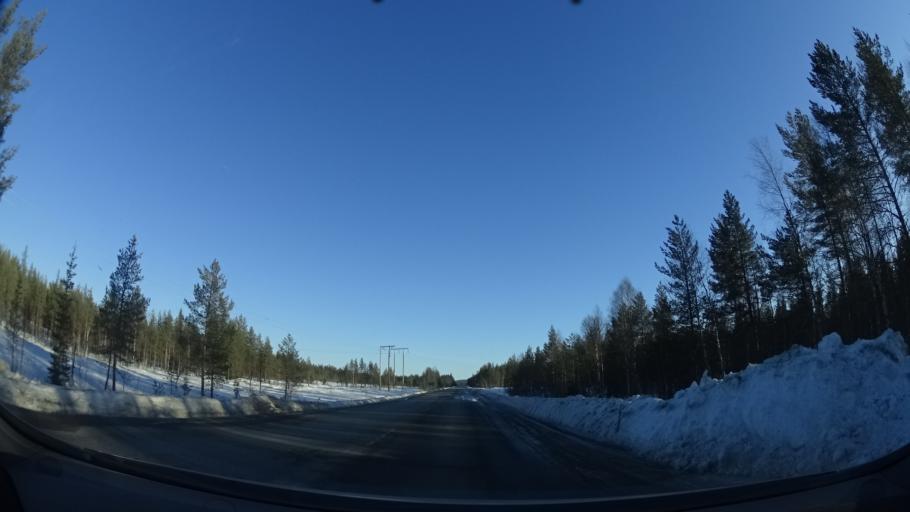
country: SE
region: Vaesterbotten
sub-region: Skelleftea Kommun
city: Langsele
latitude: 65.0513
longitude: 20.0617
